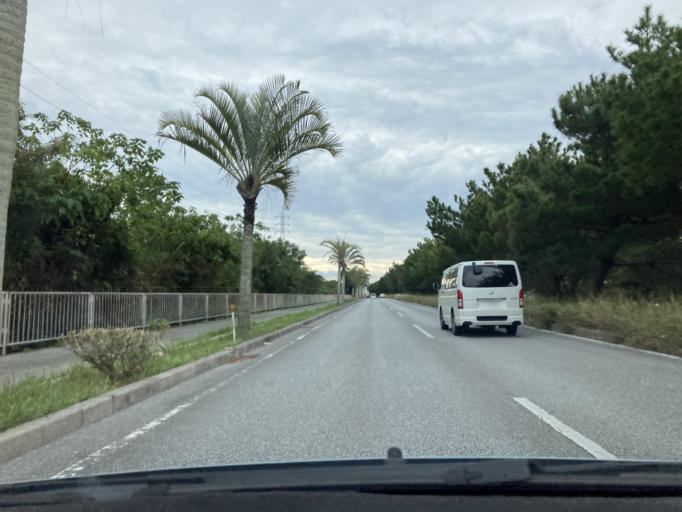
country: JP
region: Okinawa
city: Okinawa
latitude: 26.3901
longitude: 127.7551
